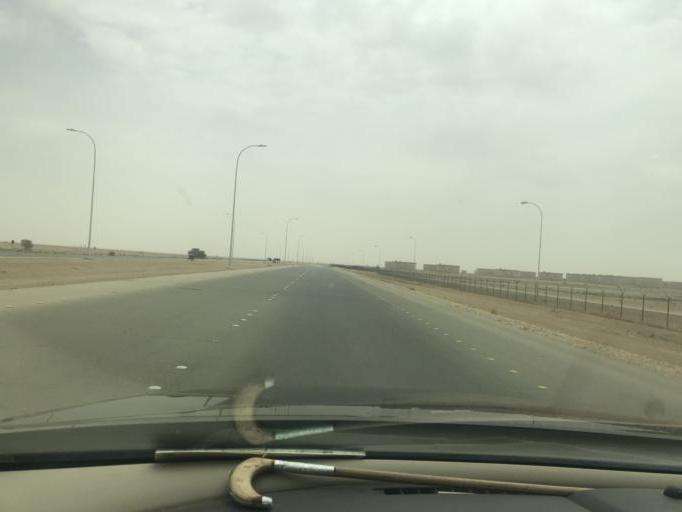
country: SA
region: Ar Riyad
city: Riyadh
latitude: 24.9819
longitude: 46.6666
